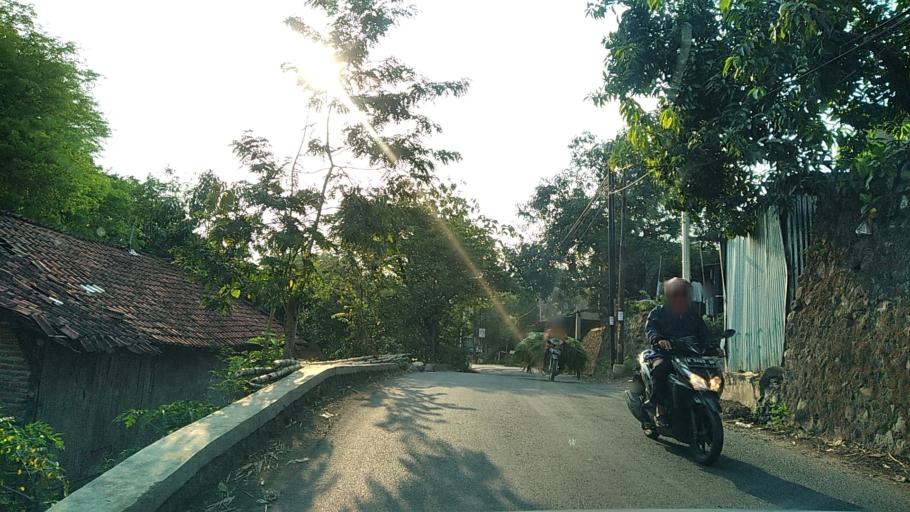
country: ID
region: Central Java
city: Mranggen
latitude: -7.0569
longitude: 110.4663
